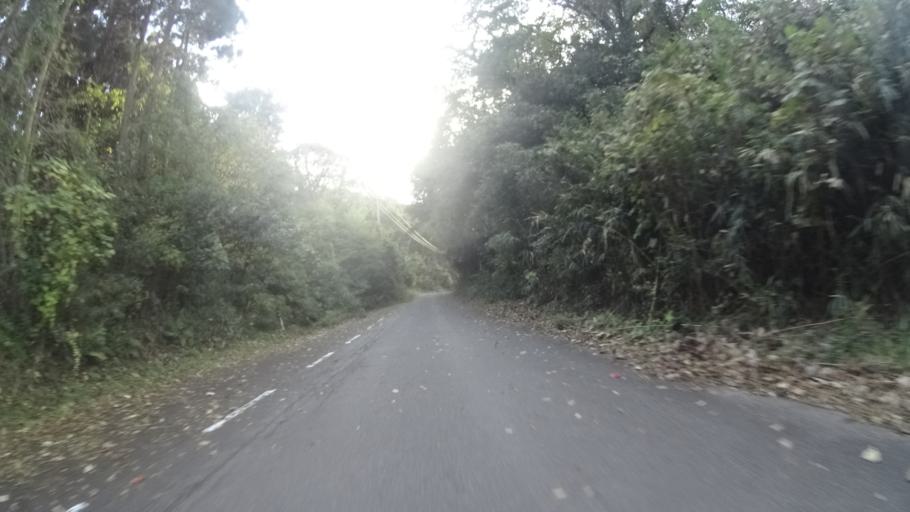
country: JP
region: Ishikawa
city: Nanao
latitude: 37.2130
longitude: 136.6932
